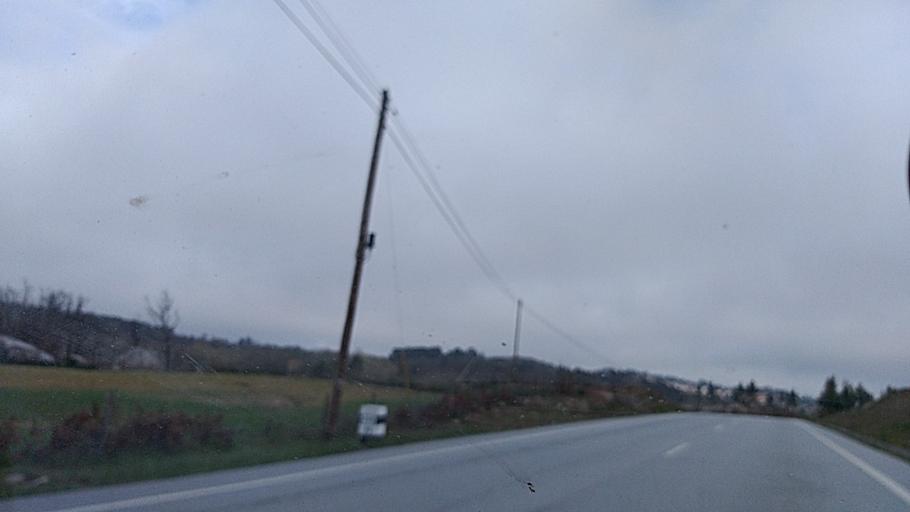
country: PT
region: Guarda
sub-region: Fornos de Algodres
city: Fornos de Algodres
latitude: 40.6713
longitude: -7.4738
